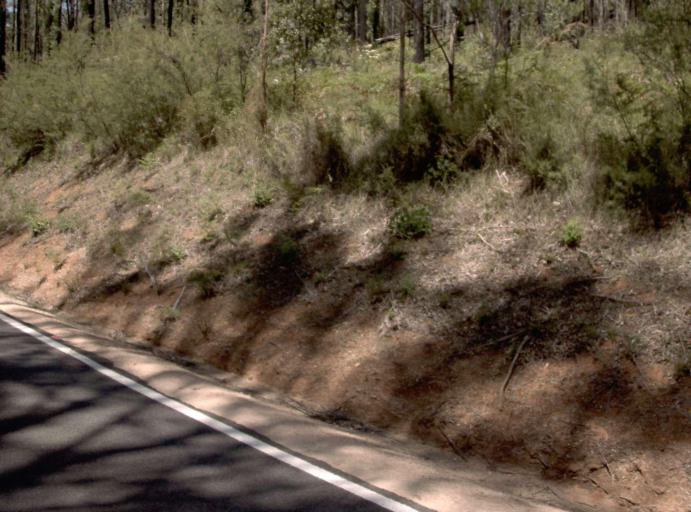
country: AU
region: New South Wales
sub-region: Bombala
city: Bombala
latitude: -37.6353
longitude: 148.8666
